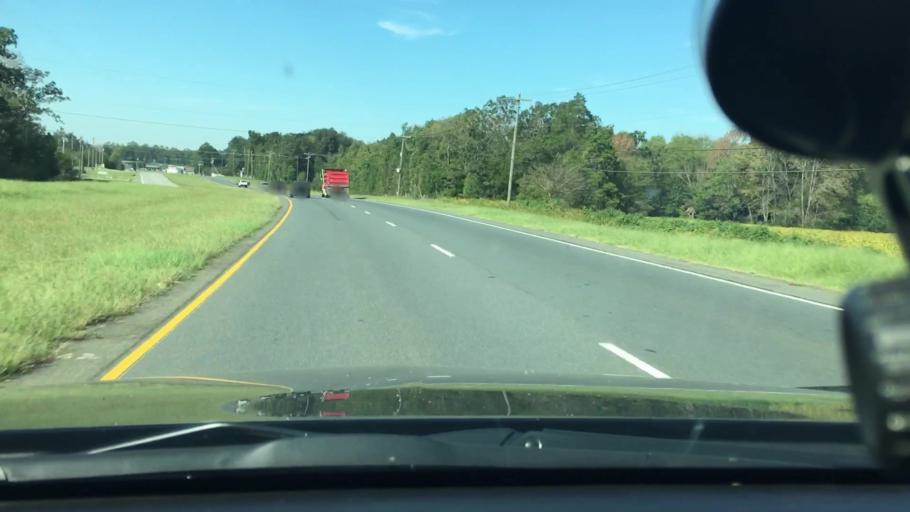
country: US
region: North Carolina
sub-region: Cabarrus County
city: Midland
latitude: 35.2491
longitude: -80.5752
